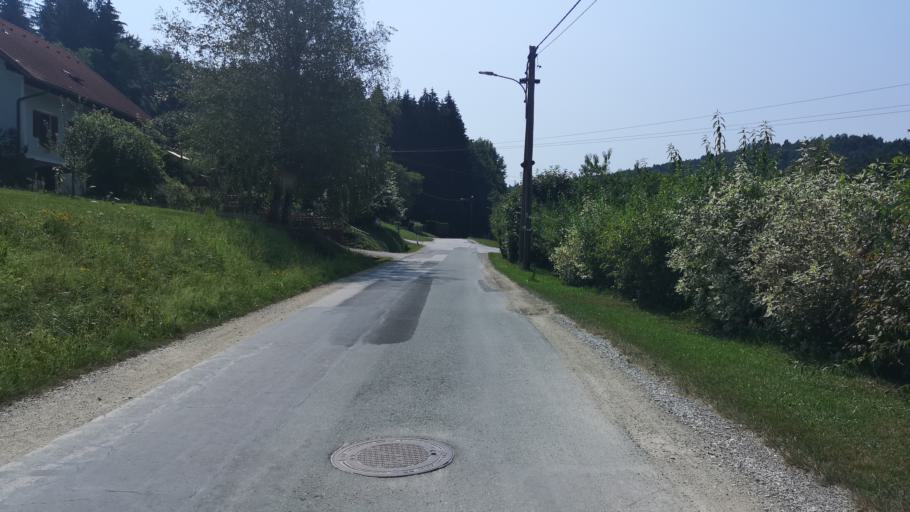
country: AT
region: Styria
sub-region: Politischer Bezirk Deutschlandsberg
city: Sankt Josef (Weststeiermark)
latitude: 46.8943
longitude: 15.3656
